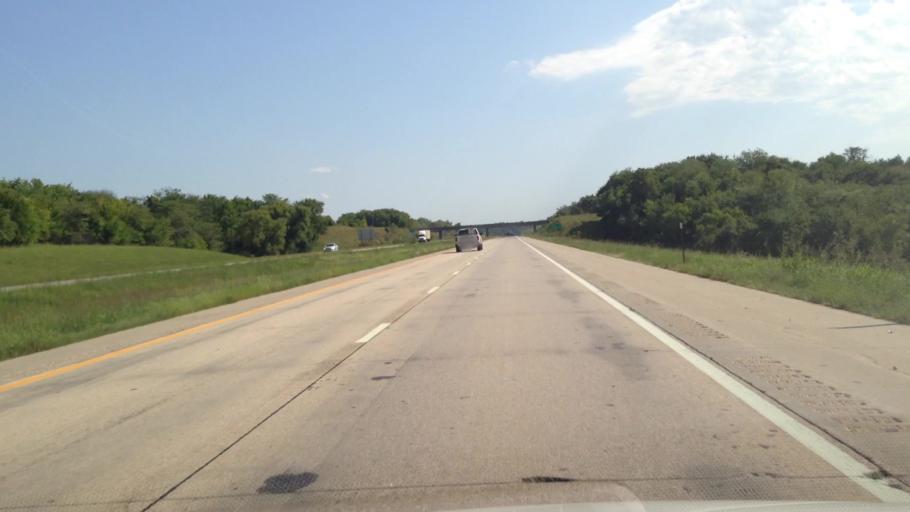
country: US
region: Kansas
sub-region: Miami County
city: Louisburg
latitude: 38.6118
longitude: -94.6947
